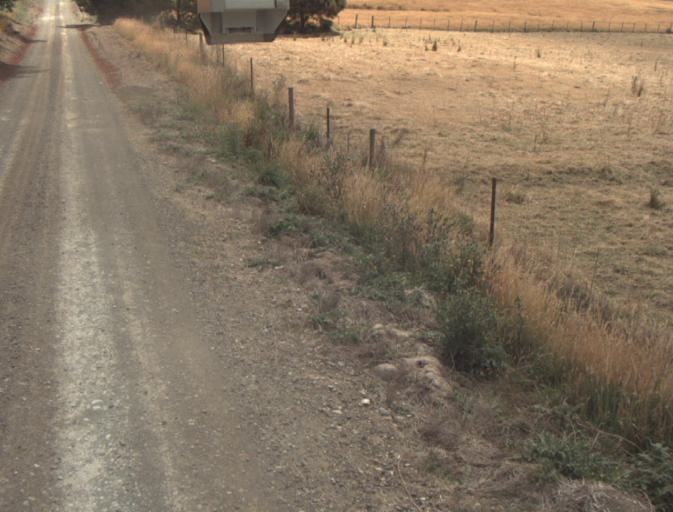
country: AU
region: Tasmania
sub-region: Launceston
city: Mayfield
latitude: -41.1973
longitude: 147.1696
